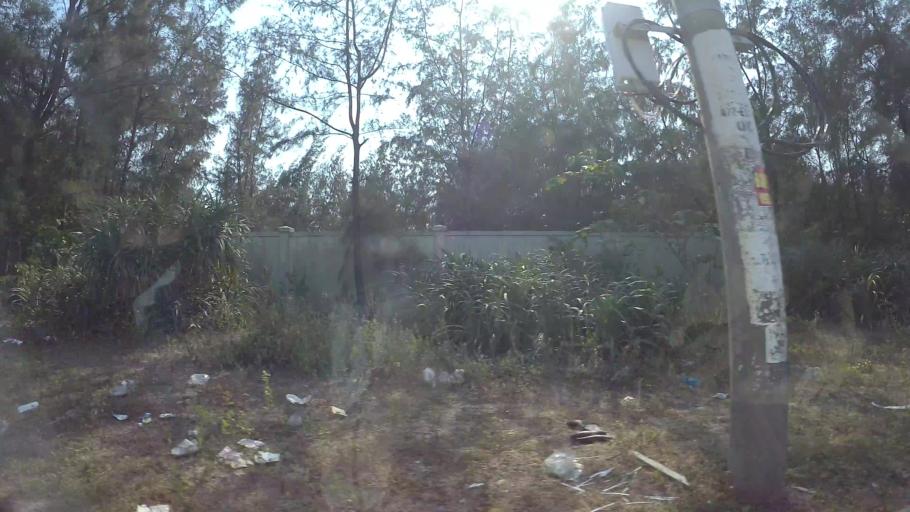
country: VN
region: Da Nang
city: Ngu Hanh Son
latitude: 15.9707
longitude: 108.2822
